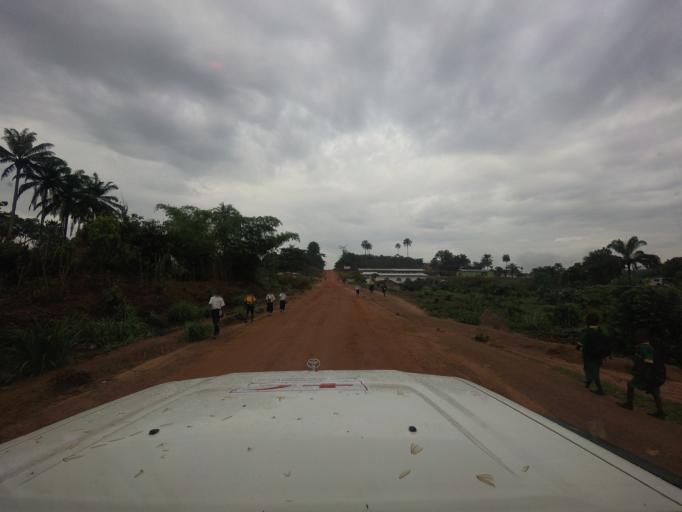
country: LR
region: Lofa
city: Voinjama
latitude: 8.4192
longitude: -9.7587
